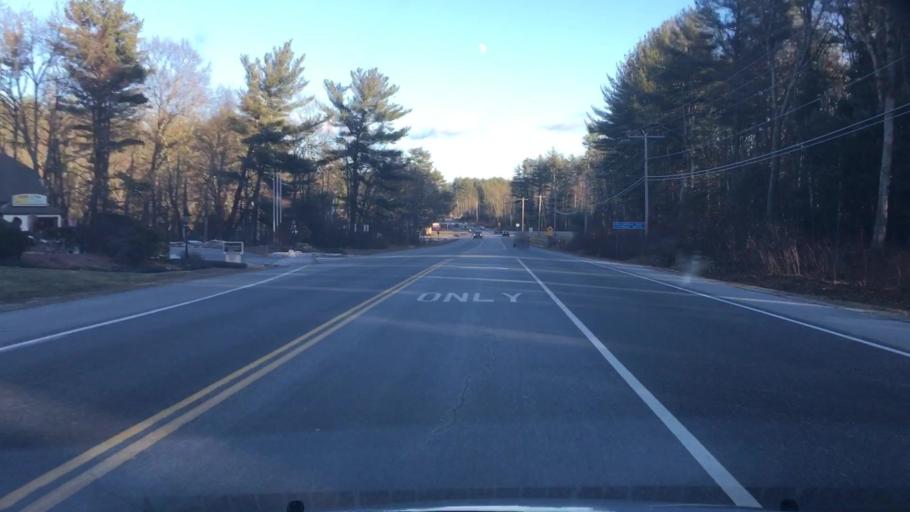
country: US
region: New Hampshire
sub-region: Hillsborough County
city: Mont Vernon
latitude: 42.8982
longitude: -71.5982
